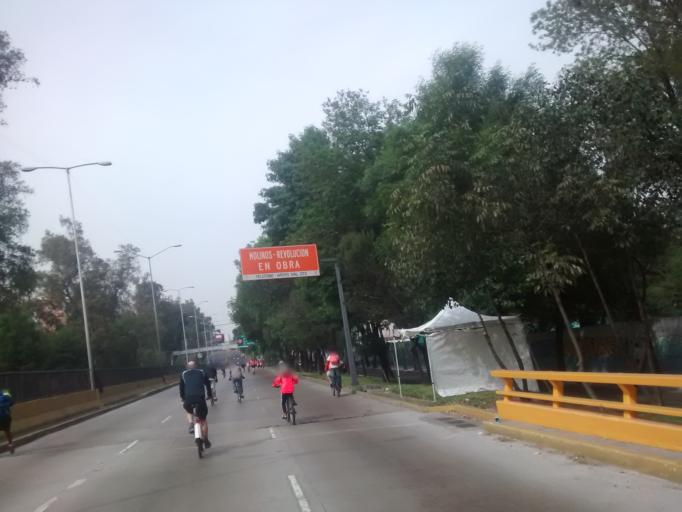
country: MX
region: Mexico City
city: Coyoacan
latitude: 19.3584
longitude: -99.1654
